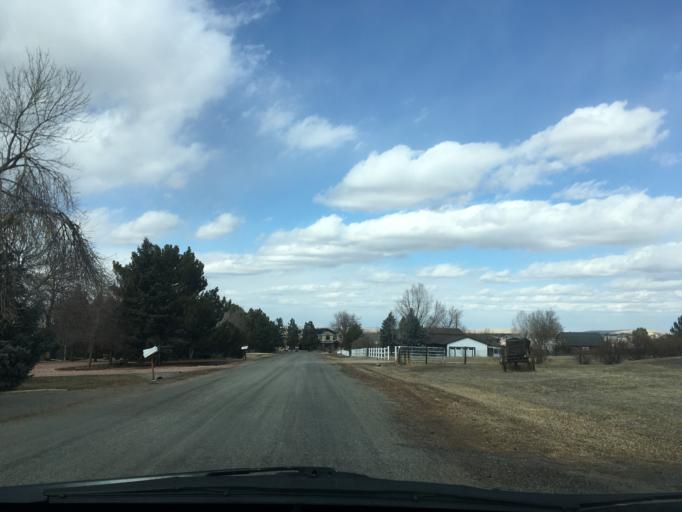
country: US
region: Colorado
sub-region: Boulder County
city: Lafayette
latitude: 39.9610
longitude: -105.0552
